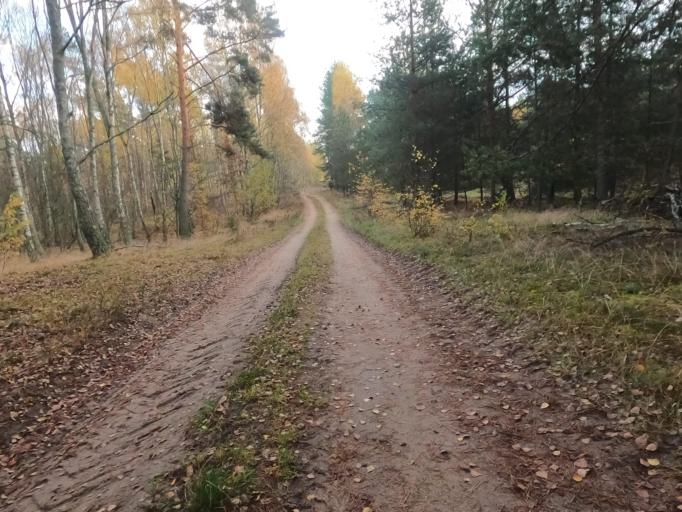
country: PL
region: West Pomeranian Voivodeship
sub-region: Powiat szczecinecki
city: Lubowo
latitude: 53.5430
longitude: 16.4337
